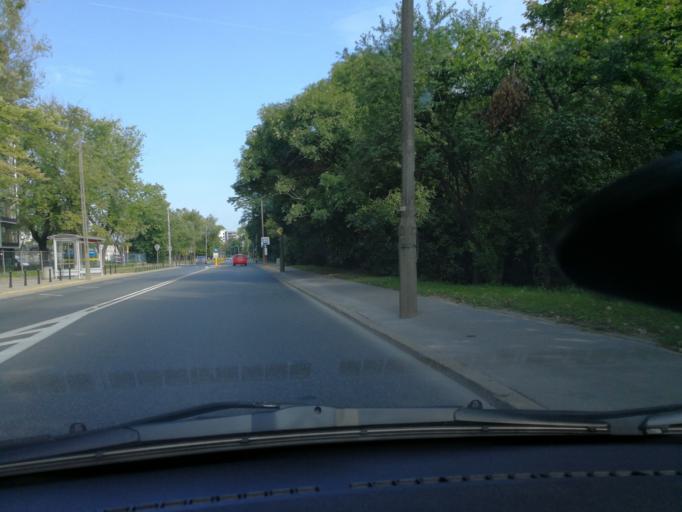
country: PL
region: Masovian Voivodeship
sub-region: Warszawa
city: Bemowo
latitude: 52.2299
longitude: 20.9423
